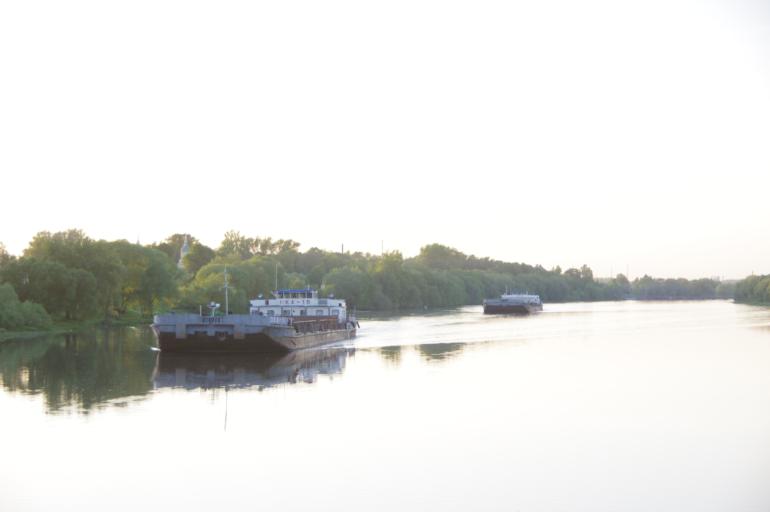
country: RU
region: Moskovskaya
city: Peski
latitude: 55.1923
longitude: 38.7497
